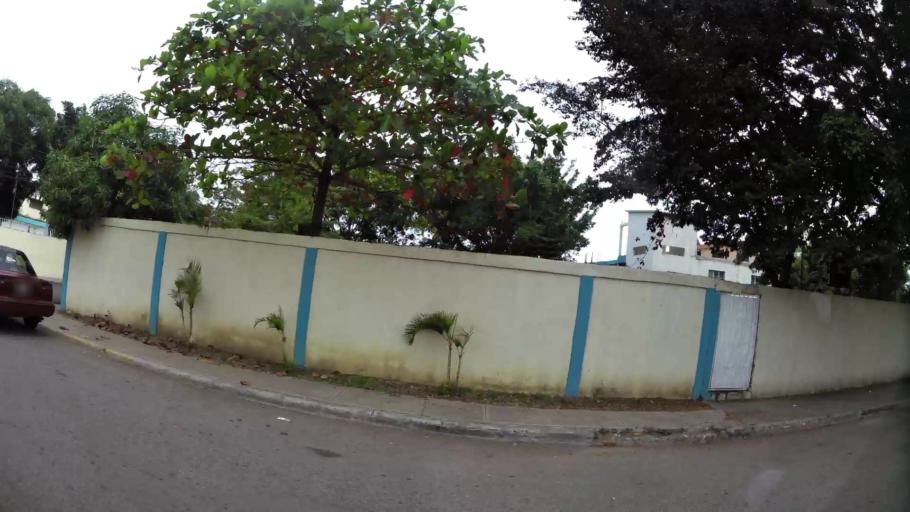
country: DO
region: Santiago
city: Santiago de los Caballeros
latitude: 19.4367
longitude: -70.6700
